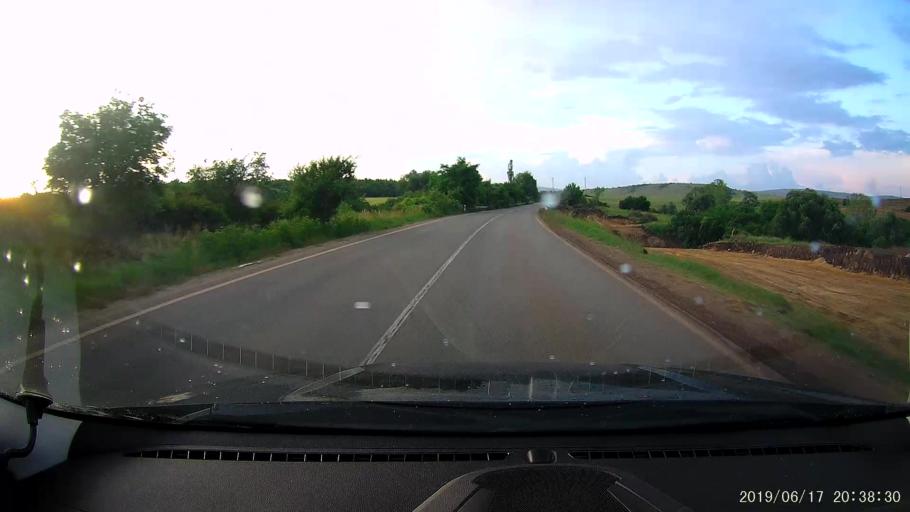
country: BG
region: Sofiya
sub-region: Obshtina Slivnitsa
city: Slivnitsa
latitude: 42.8730
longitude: 23.0183
